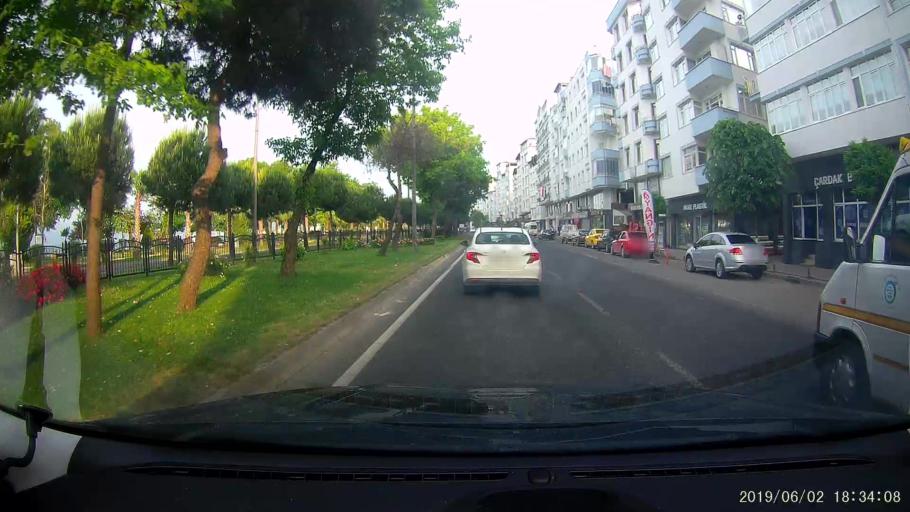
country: TR
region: Ordu
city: Fatsa
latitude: 41.0310
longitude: 37.5012
